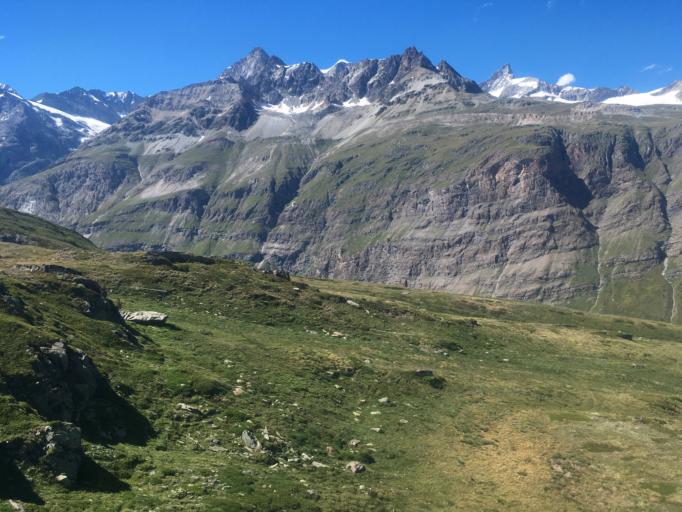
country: CH
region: Valais
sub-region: Visp District
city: Zermatt
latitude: 45.9963
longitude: 7.7154
